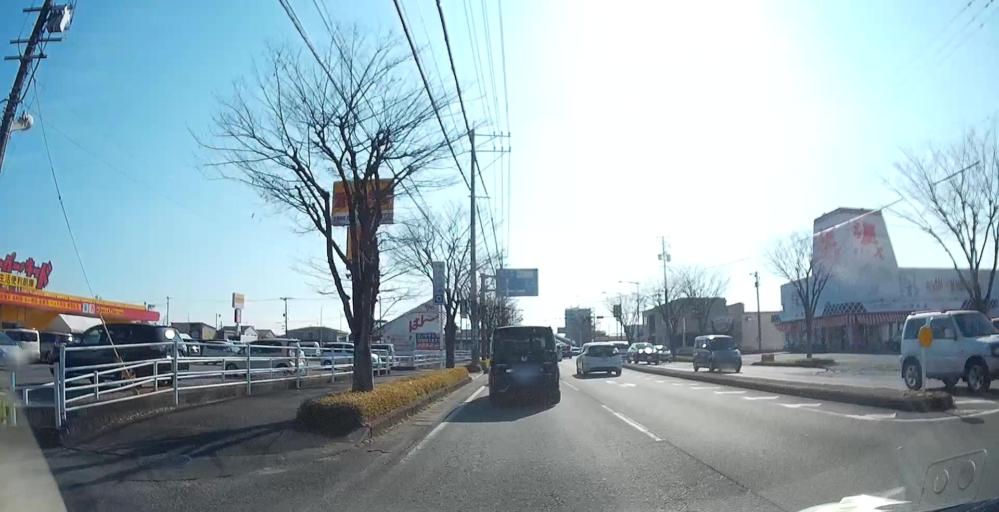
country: JP
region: Kumamoto
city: Kumamoto
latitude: 32.7770
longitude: 130.6731
